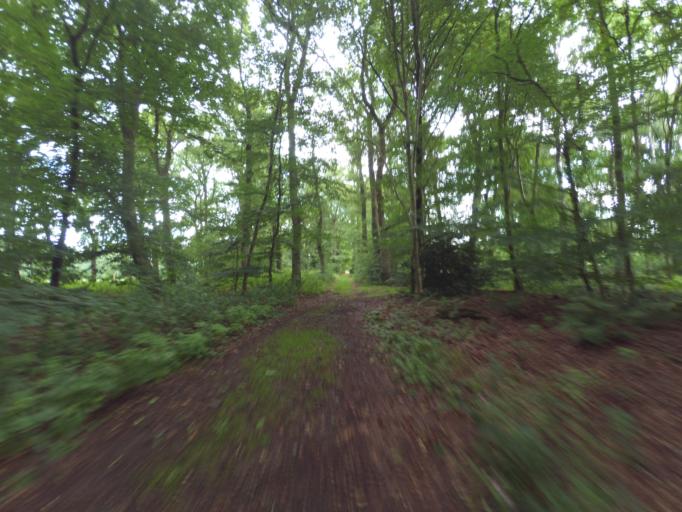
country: NL
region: Utrecht
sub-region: Gemeente Utrechtse Heuvelrug
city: Maarsbergen
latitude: 52.0506
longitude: 5.4052
